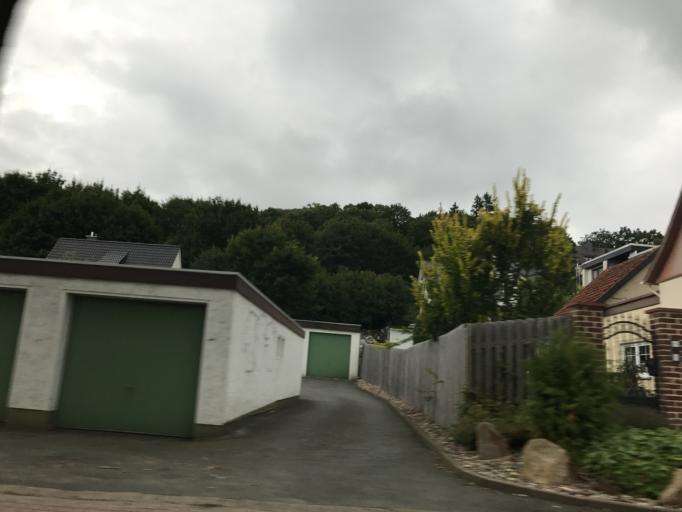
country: DE
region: Lower Saxony
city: Bad Harzburg
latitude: 51.8849
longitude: 10.5689
